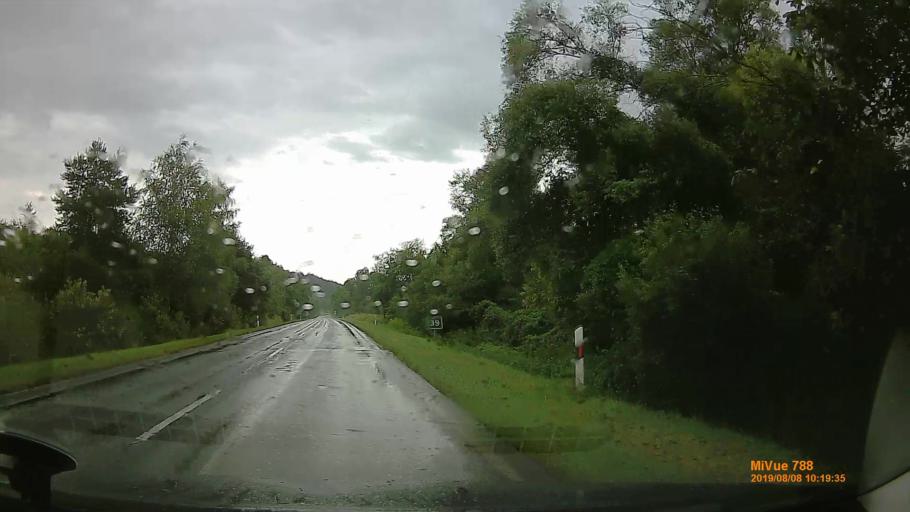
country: HU
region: Zala
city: Zalaegerszeg
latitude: 46.7626
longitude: 16.8576
